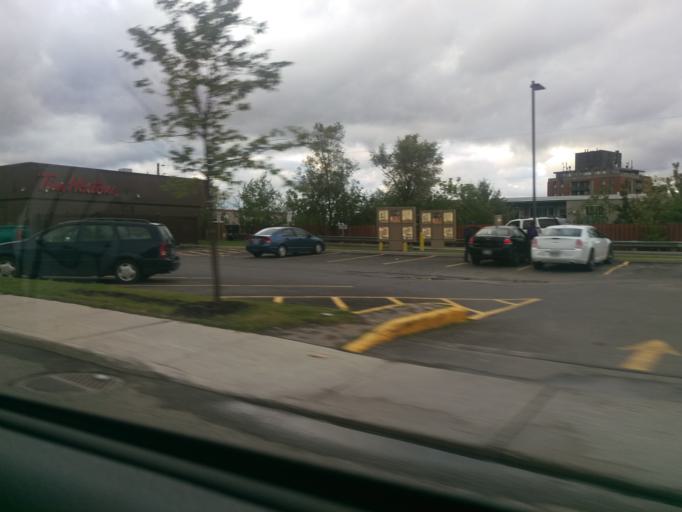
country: CA
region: Quebec
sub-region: Outaouais
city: Gatineau
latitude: 45.4516
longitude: -75.7379
